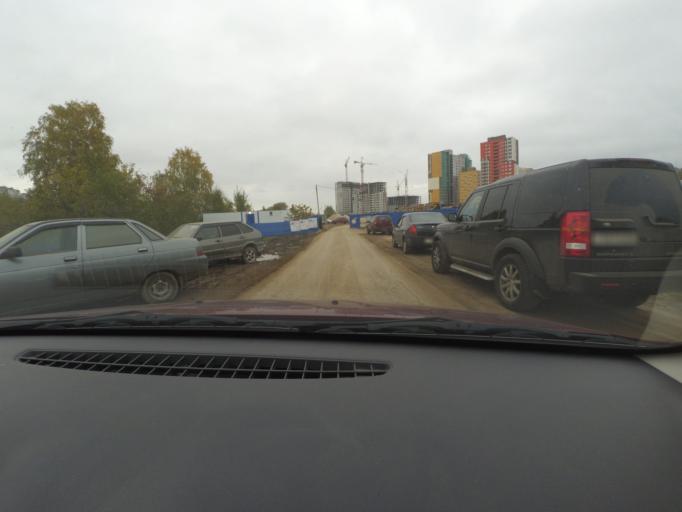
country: RU
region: Nizjnij Novgorod
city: Afonino
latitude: 56.2777
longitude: 44.0441
